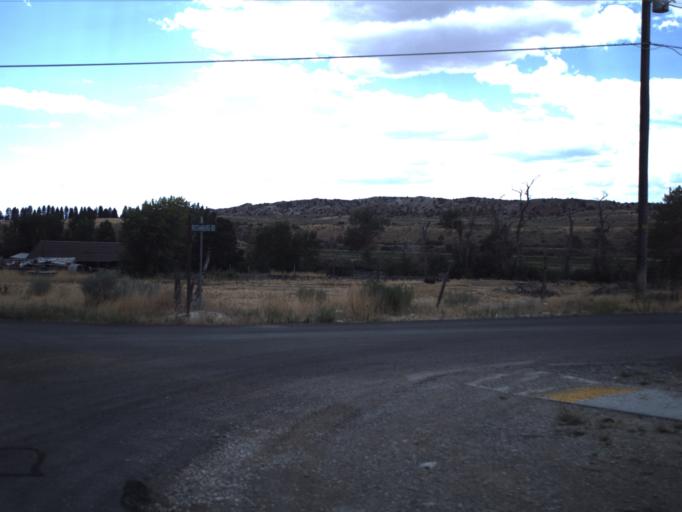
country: US
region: Utah
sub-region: Sanpete County
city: Centerfield
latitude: 39.1245
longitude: -111.7115
